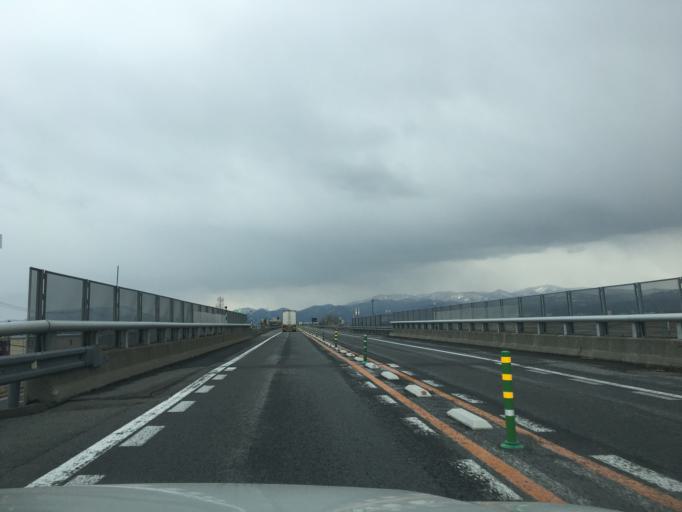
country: JP
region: Aomori
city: Aomori Shi
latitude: 40.7977
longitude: 140.7187
